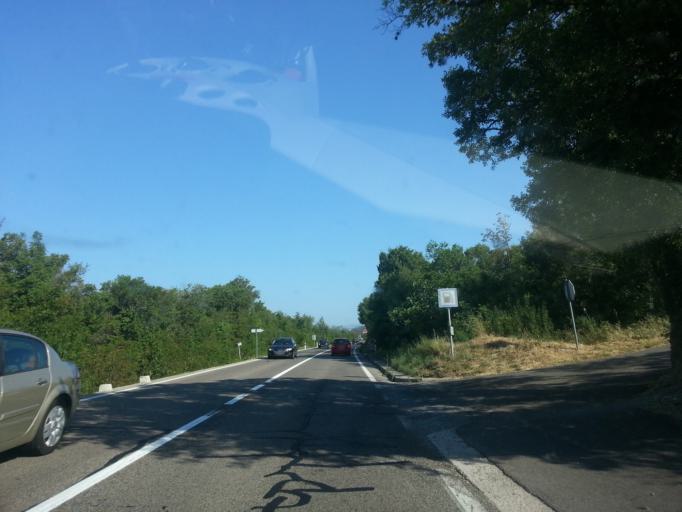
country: HR
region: Primorsko-Goranska
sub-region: Grad Crikvenica
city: Jadranovo
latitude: 45.2209
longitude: 14.6386
